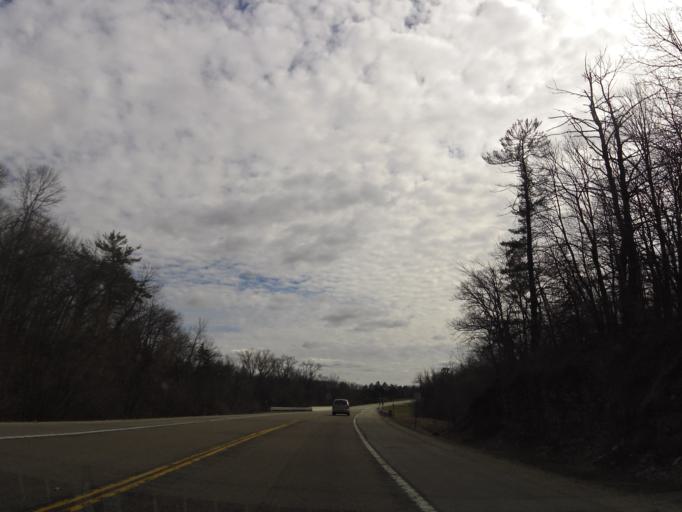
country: US
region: Minnesota
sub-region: Olmsted County
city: Stewartville
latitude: 43.8922
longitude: -92.4083
